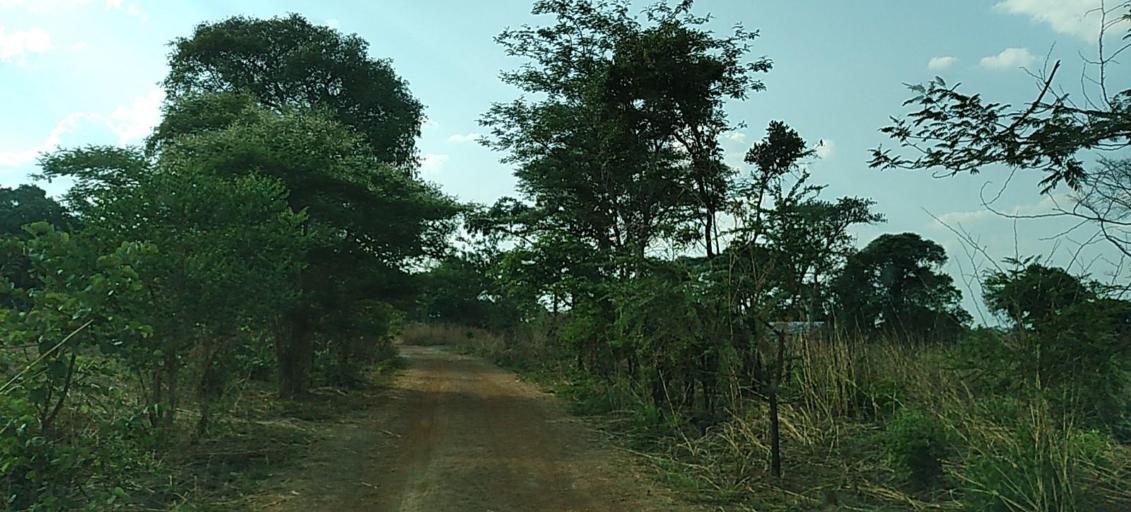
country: ZM
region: Copperbelt
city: Mpongwe
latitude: -13.4733
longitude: 28.0734
